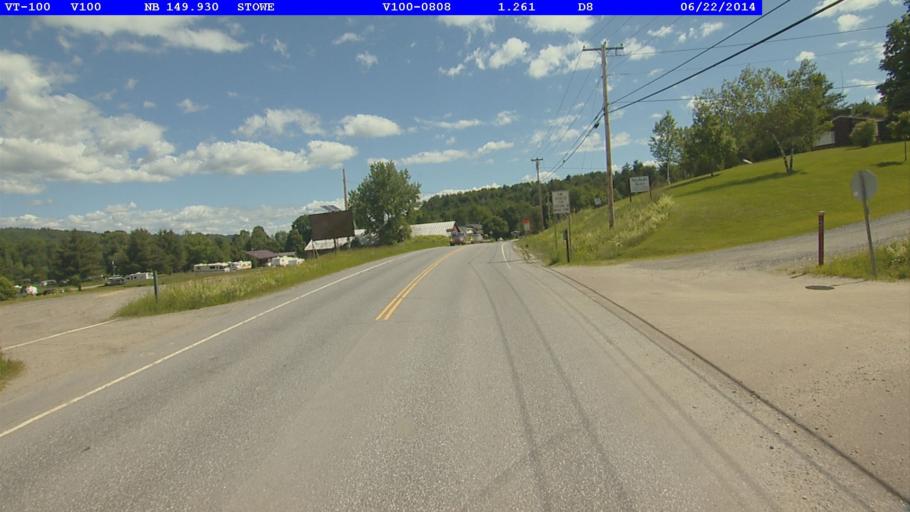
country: US
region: Vermont
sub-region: Washington County
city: Waterbury
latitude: 44.4408
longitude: -72.7072
